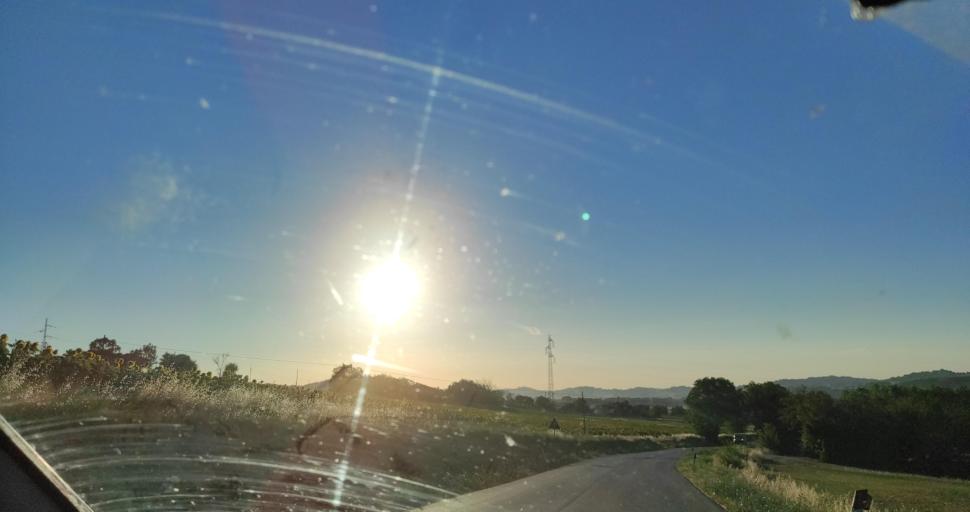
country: IT
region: The Marches
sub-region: Provincia di Macerata
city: Casette Verdini
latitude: 43.2291
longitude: 13.3980
